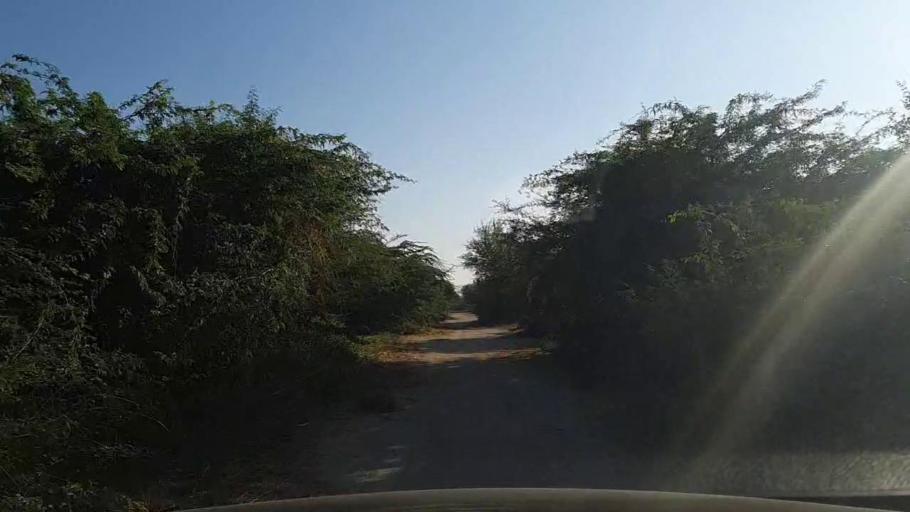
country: PK
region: Sindh
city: Mirpur Batoro
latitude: 24.6741
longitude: 68.3644
